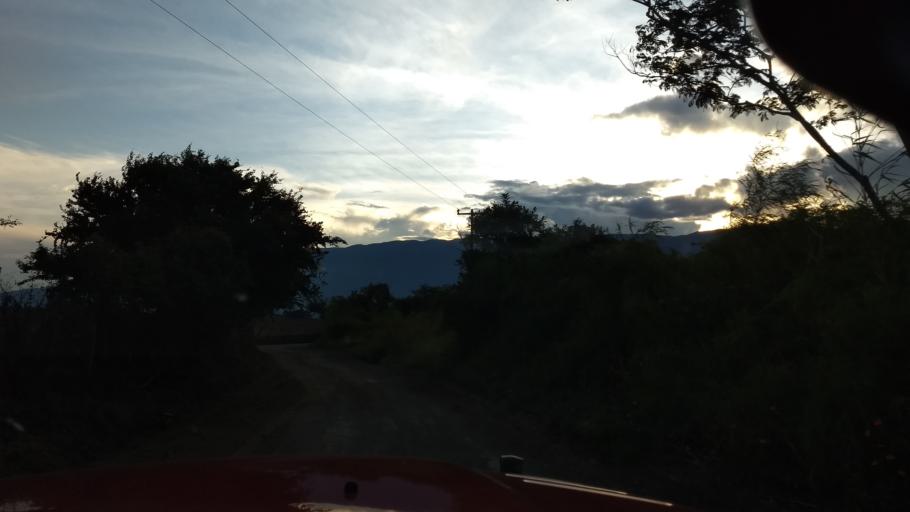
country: MX
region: Colima
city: Suchitlan
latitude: 19.4926
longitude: -103.7844
